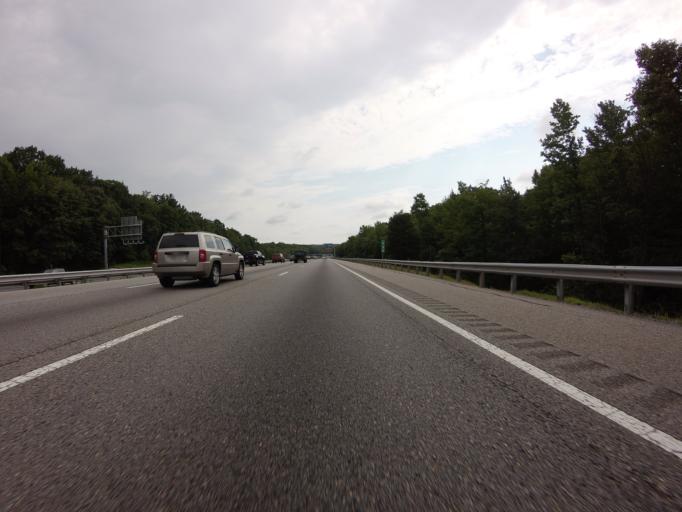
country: US
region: Maryland
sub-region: Cecil County
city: Perryville
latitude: 39.6017
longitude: -76.0417
